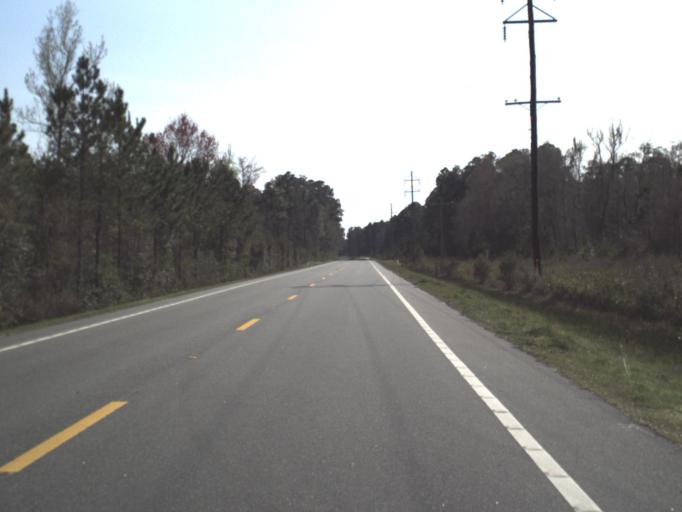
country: US
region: Florida
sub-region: Wakulla County
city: Crawfordville
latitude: 30.0093
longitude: -84.5026
